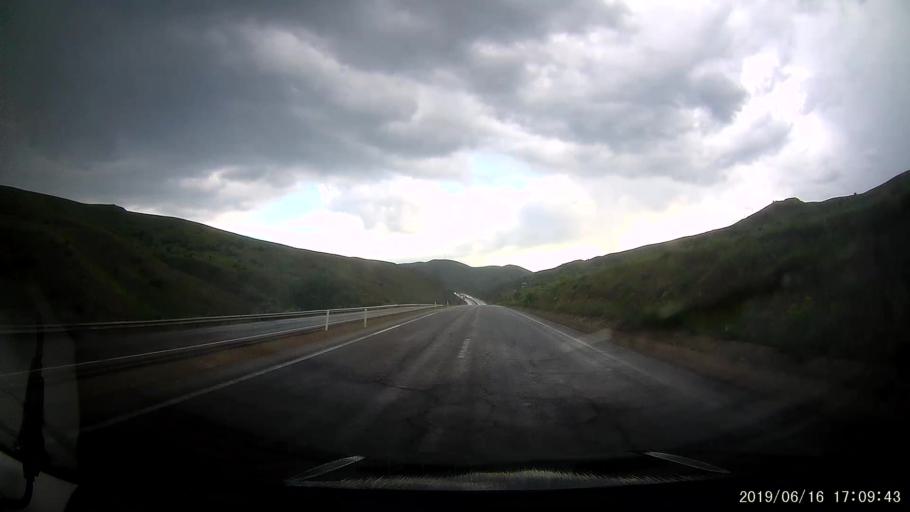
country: TR
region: Erzurum
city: Askale
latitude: 39.8905
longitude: 40.6480
